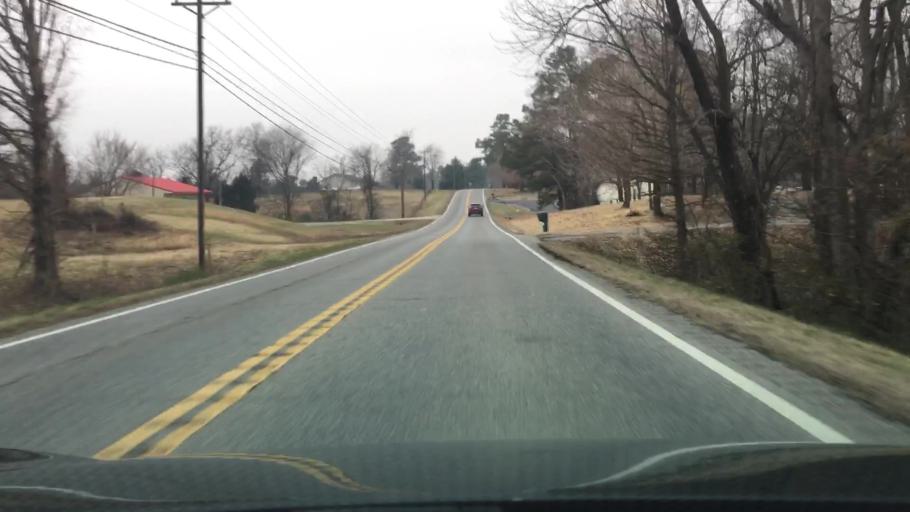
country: US
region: Kentucky
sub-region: Livingston County
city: Ledbetter
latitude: 36.9669
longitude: -88.4481
